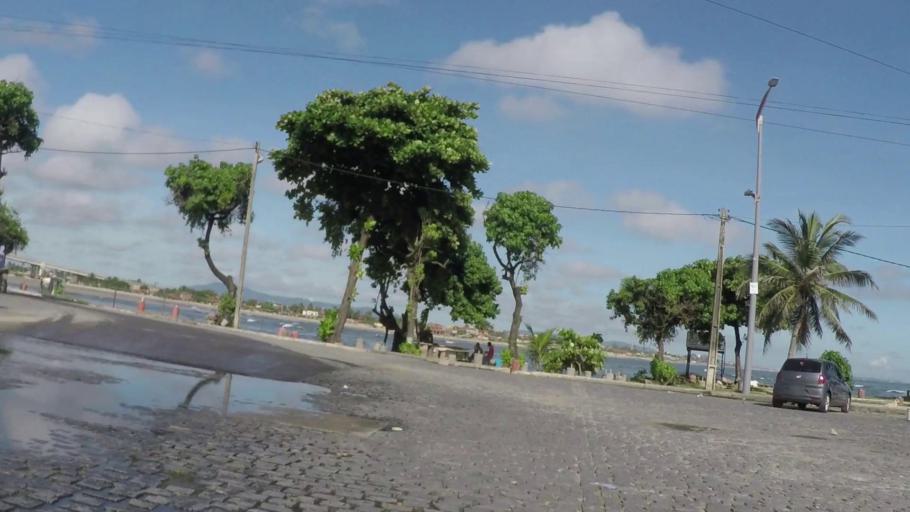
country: BR
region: Ceara
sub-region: Fortaleza
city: Fortaleza
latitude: -3.6945
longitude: -38.5863
